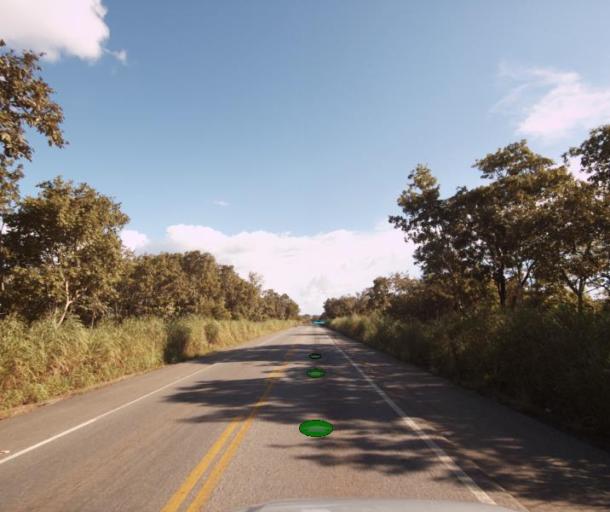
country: BR
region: Goias
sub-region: Porangatu
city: Porangatu
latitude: -13.0648
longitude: -49.1833
